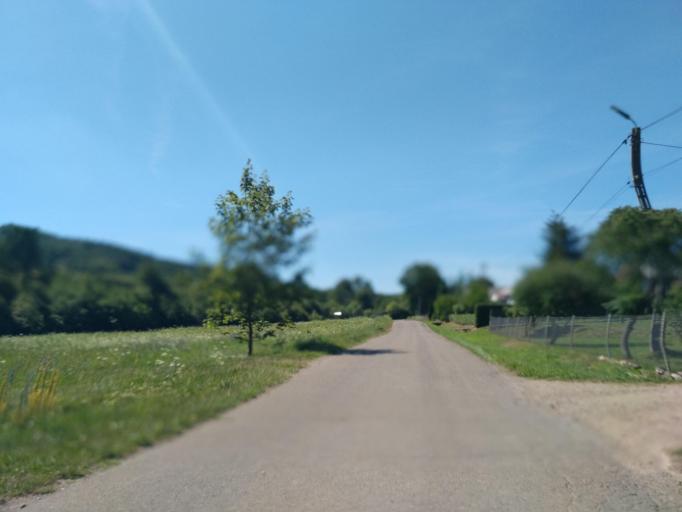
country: PL
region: Subcarpathian Voivodeship
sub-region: Powiat sanocki
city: Nowosielce-Gniewosz
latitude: 49.5291
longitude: 22.0443
